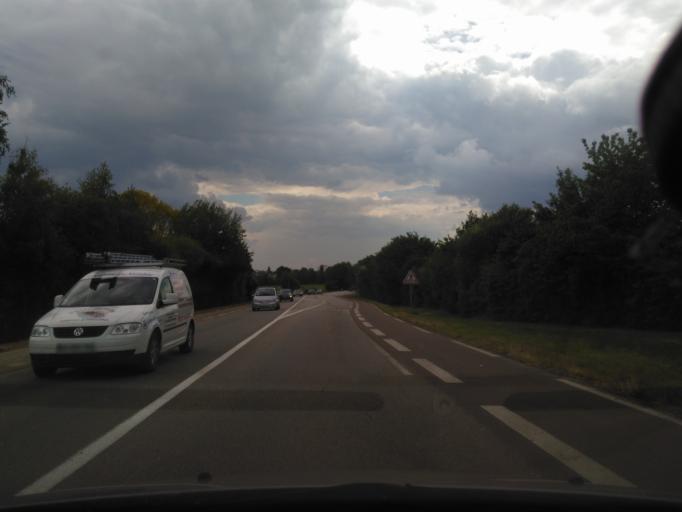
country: FR
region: Pays de la Loire
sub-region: Departement de la Vendee
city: La Roche-sur-Yon
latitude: 46.6910
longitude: -1.4246
